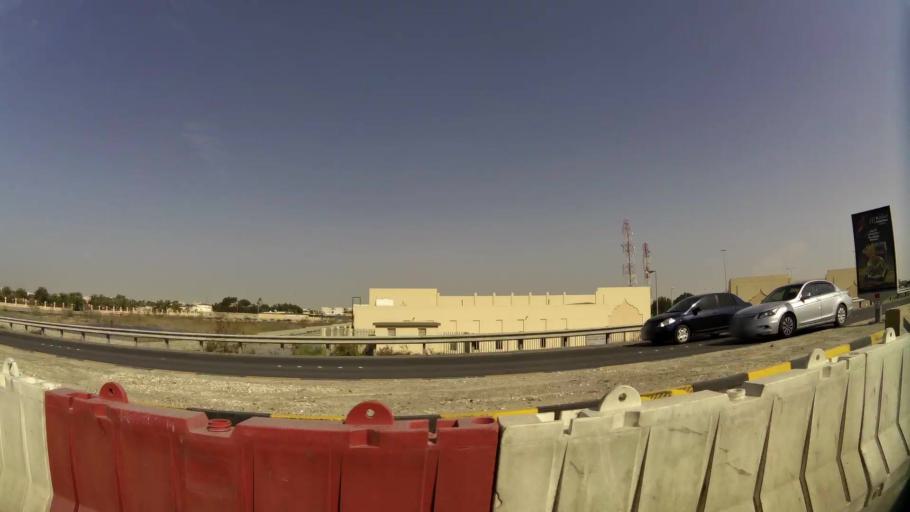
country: BH
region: Central Governorate
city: Madinat Hamad
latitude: 26.1755
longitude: 50.4655
